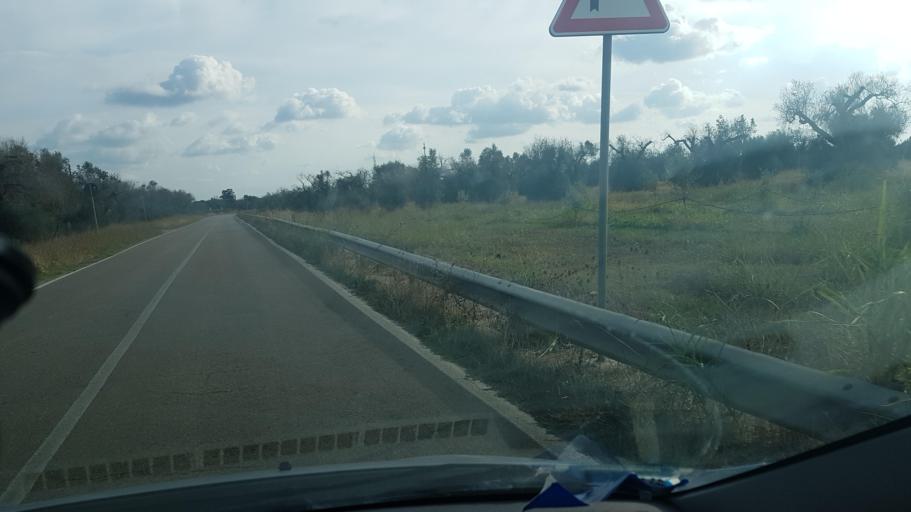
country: IT
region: Apulia
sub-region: Provincia di Brindisi
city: Cellino San Marco
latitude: 40.4517
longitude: 17.9551
